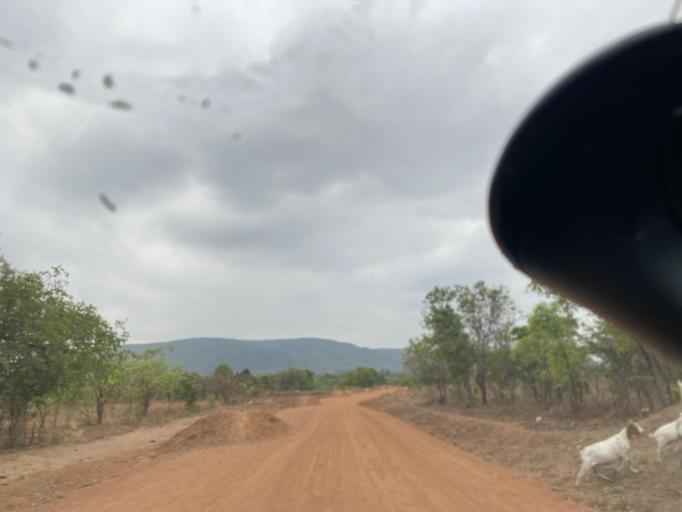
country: ZM
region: Lusaka
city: Chongwe
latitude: -15.2007
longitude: 28.7630
